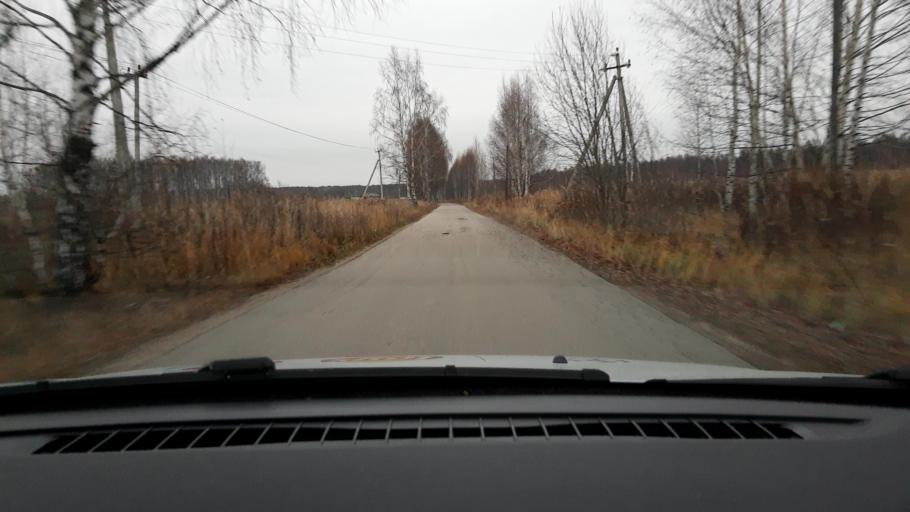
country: RU
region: Nizjnij Novgorod
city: Neklyudovo
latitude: 56.4131
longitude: 44.0124
